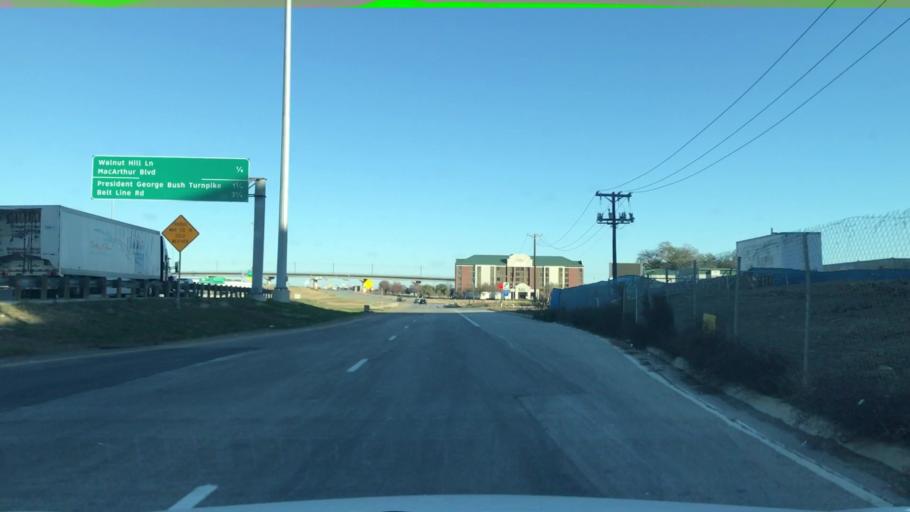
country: US
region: Texas
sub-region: Dallas County
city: Irving
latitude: 32.8757
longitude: -96.9458
